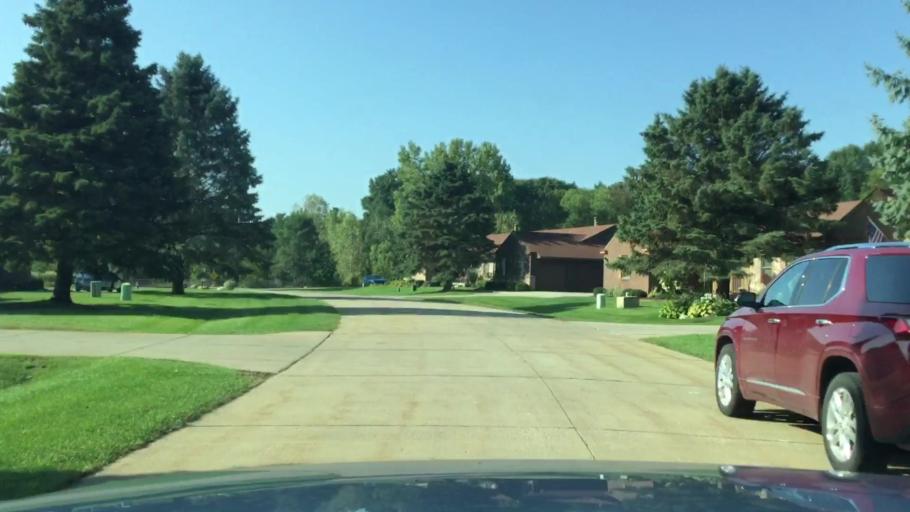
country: US
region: Michigan
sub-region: Livingston County
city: Whitmore Lake
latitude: 42.4568
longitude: -83.7089
